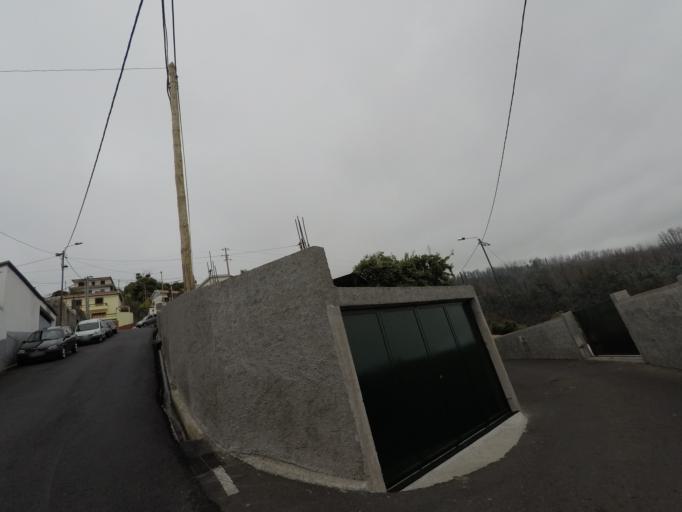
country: PT
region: Madeira
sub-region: Funchal
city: Nossa Senhora do Monte
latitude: 32.6779
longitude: -16.9381
